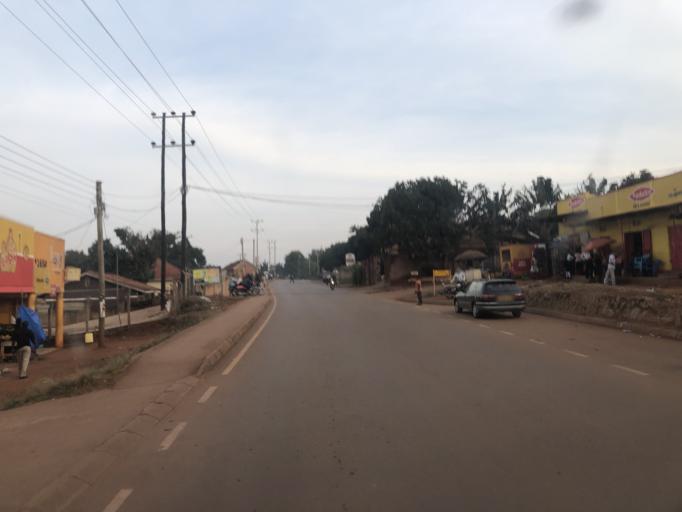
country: UG
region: Central Region
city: Kampala Central Division
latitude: 0.2865
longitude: 32.5377
